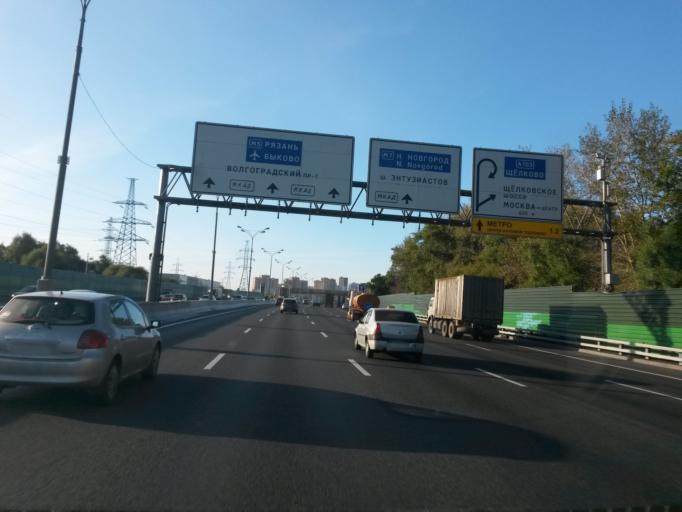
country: RU
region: Moscow
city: Gol'yanovo
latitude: 55.8220
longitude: 37.8368
